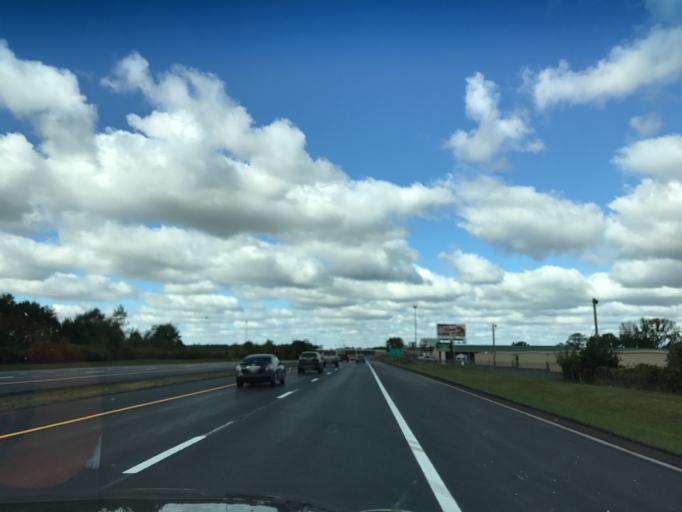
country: US
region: Ohio
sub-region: Fairfield County
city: Canal Winchester
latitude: 39.8412
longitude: -82.7715
